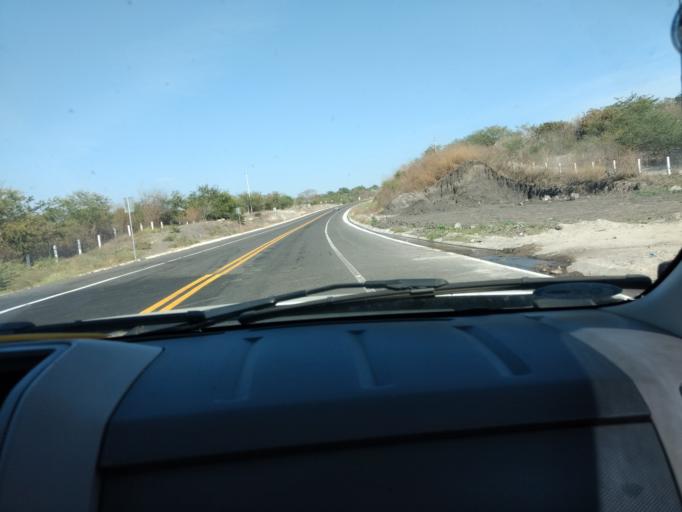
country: MX
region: Morelos
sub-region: Ayala
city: El Salitre
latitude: 18.6734
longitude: -98.9533
